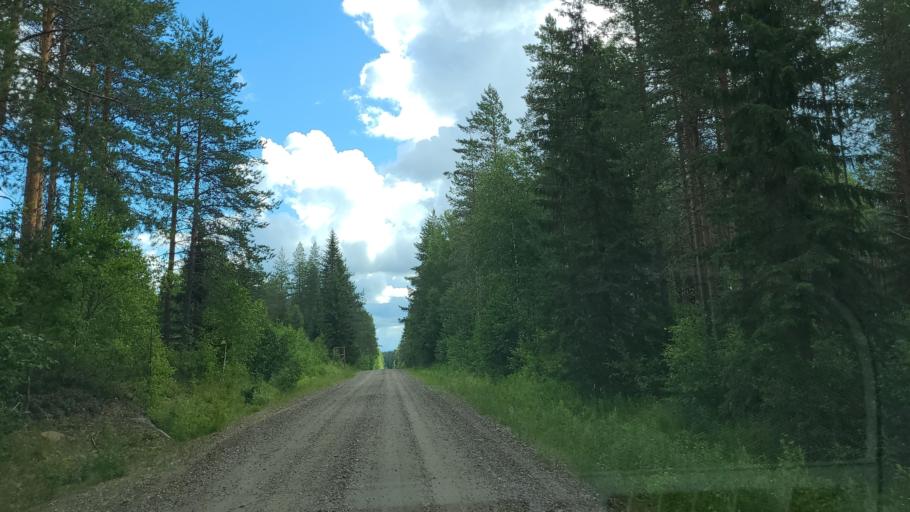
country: FI
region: Northern Savo
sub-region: Koillis-Savo
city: Kaavi
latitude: 63.0272
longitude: 28.7669
